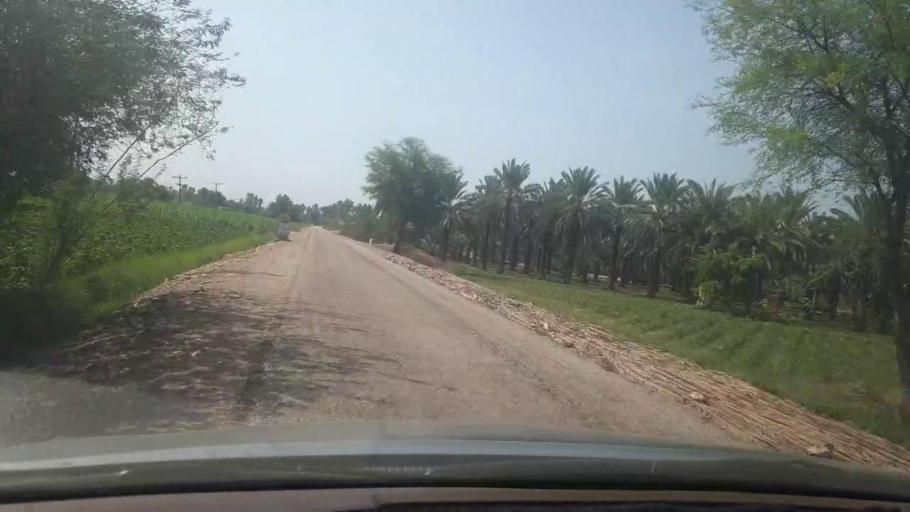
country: PK
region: Sindh
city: Ranipur
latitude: 27.2856
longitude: 68.5791
